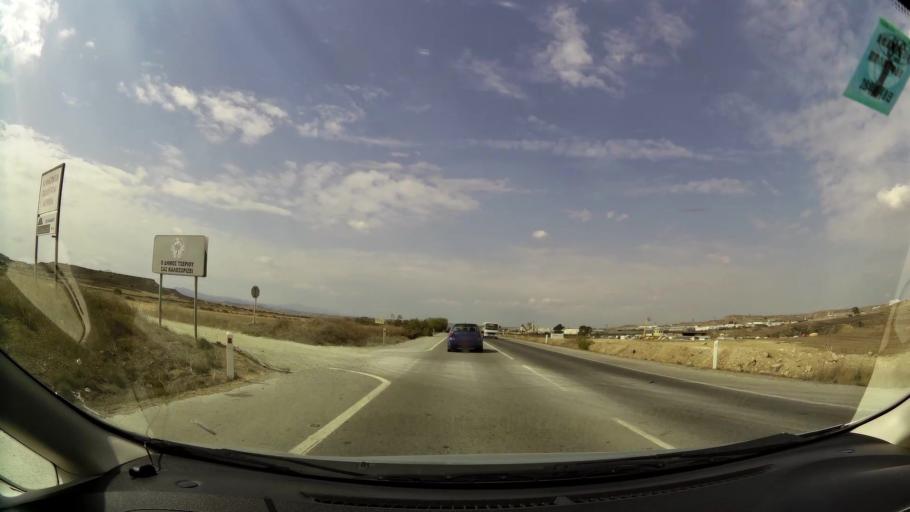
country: CY
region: Lefkosia
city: Tseri
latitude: 35.0591
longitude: 33.3642
